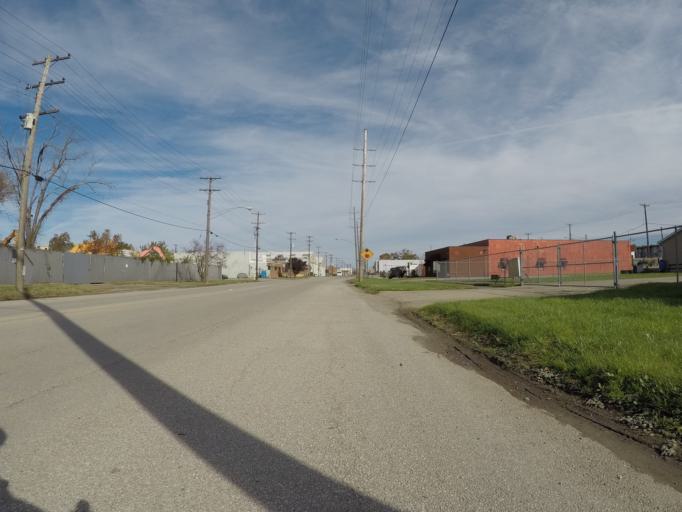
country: US
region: West Virginia
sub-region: Cabell County
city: Huntington
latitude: 38.4192
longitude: -82.4594
